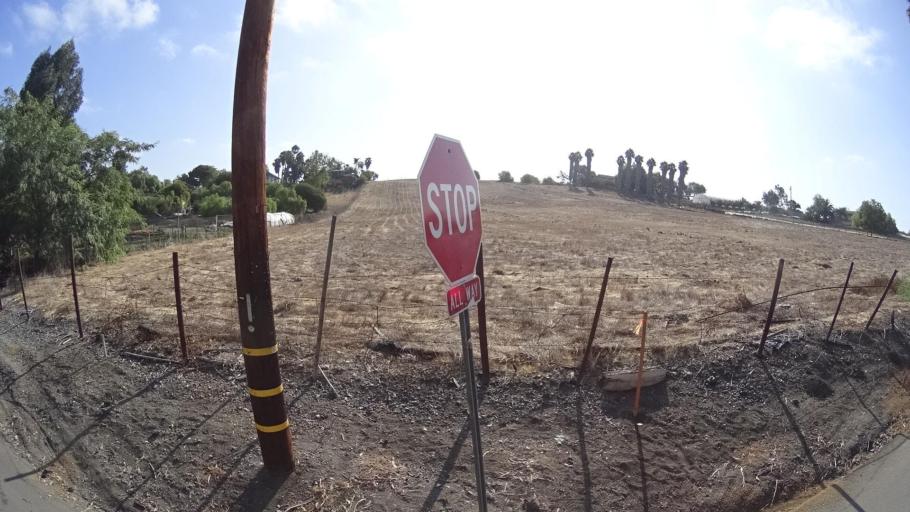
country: US
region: California
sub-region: San Diego County
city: Vista
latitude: 33.1754
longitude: -117.2473
